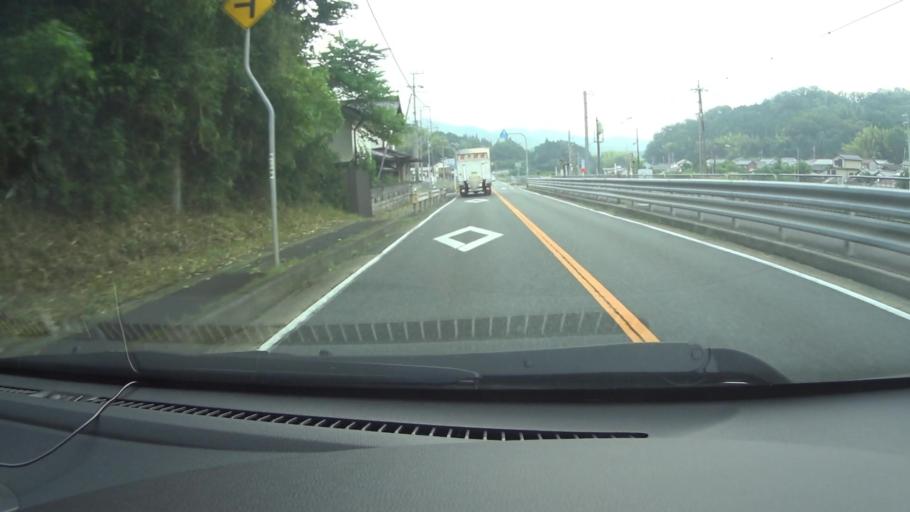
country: JP
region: Kyoto
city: Ayabe
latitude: 35.3460
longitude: 135.3117
